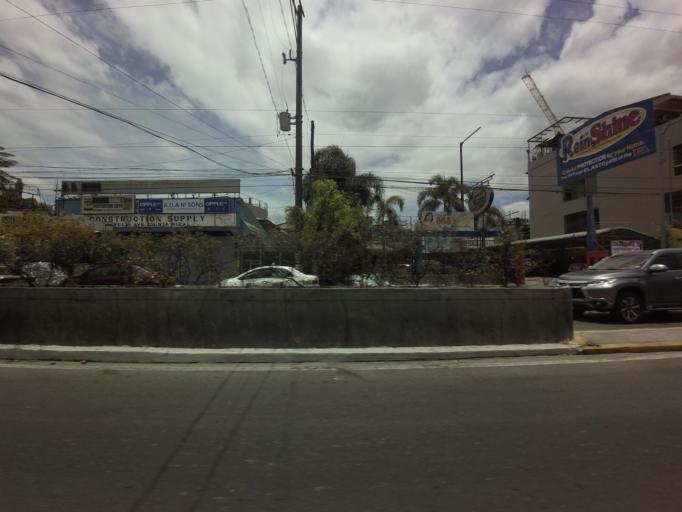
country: PH
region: Metro Manila
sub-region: Marikina
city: Calumpang
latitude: 14.6143
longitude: 121.1024
